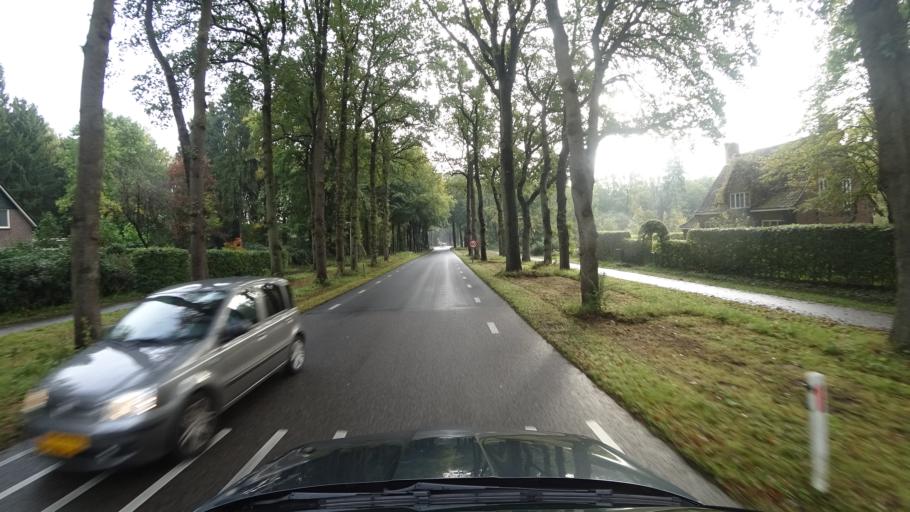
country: NL
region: Gelderland
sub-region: Gemeente Renkum
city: Renkum
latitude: 51.9916
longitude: 5.7151
